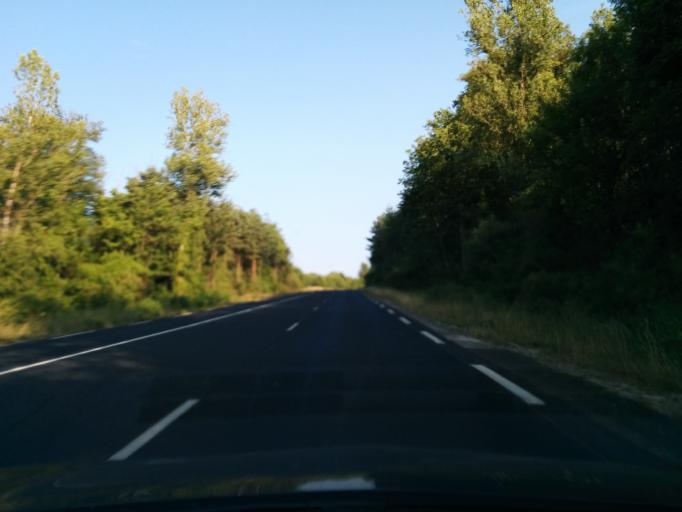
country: FR
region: Midi-Pyrenees
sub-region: Departement du Lot
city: Le Vigan
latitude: 44.7669
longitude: 1.4800
